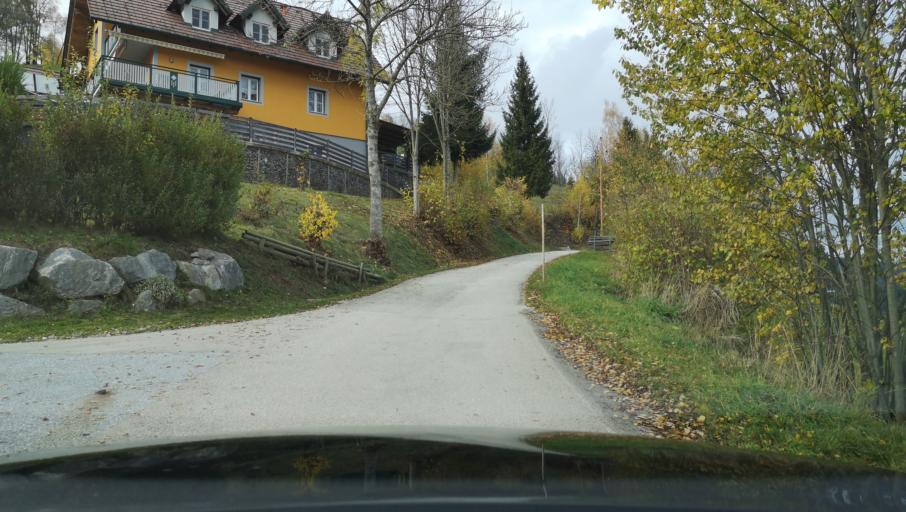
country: AT
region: Styria
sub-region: Politischer Bezirk Weiz
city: Birkfeld
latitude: 47.3653
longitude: 15.6496
